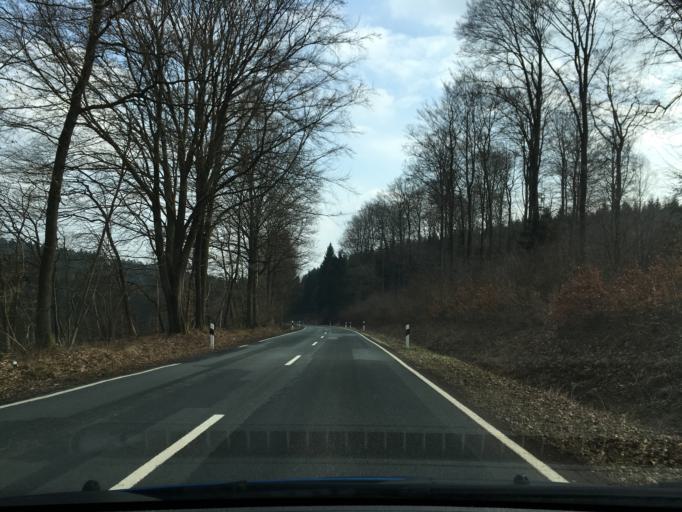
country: DE
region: Lower Saxony
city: Heinade
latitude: 51.7968
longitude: 9.6432
